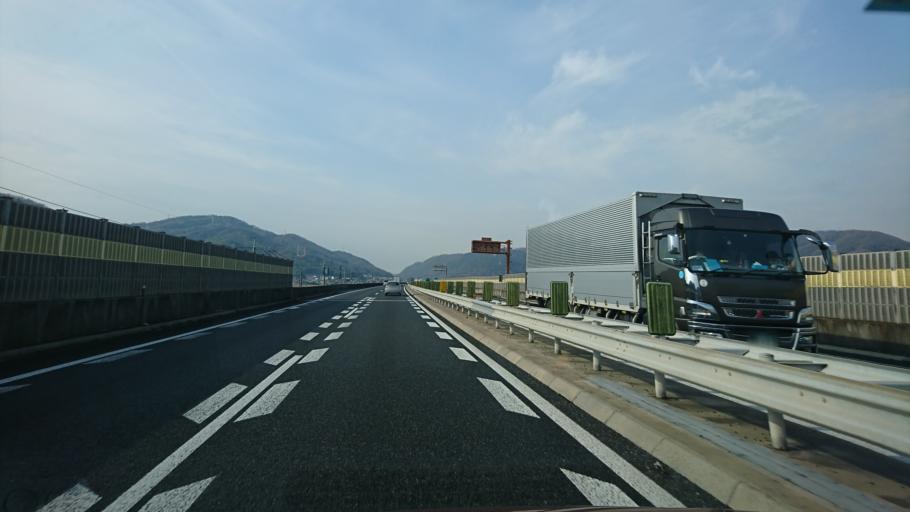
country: JP
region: Okayama
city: Okayama-shi
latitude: 34.7402
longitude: 134.0184
